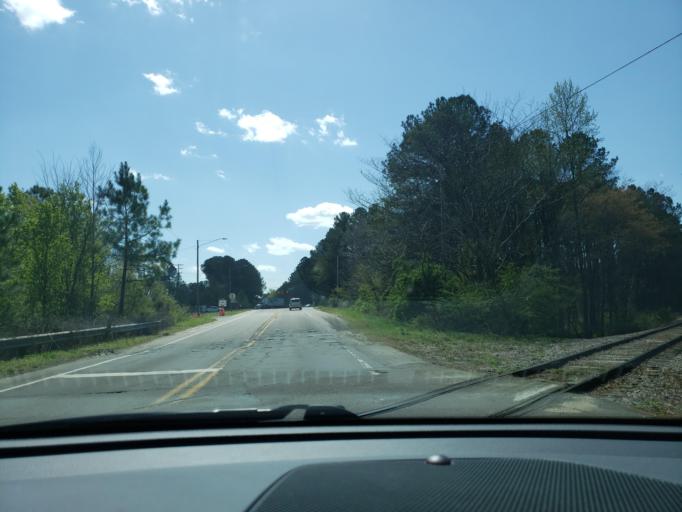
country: US
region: North Carolina
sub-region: Durham County
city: Durham
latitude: 35.9322
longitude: -78.8871
